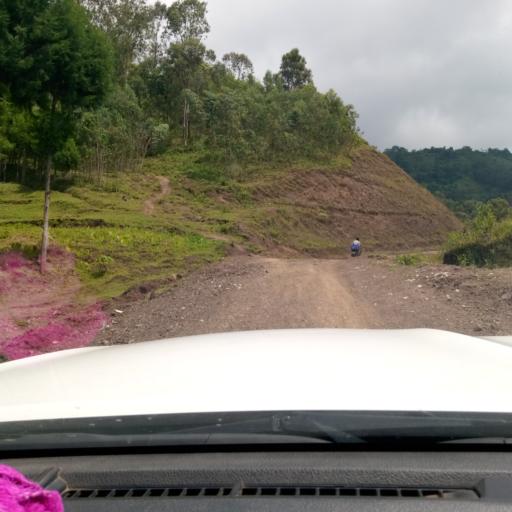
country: ET
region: Southern Nations, Nationalities, and People's Region
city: Arba Minch'
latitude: 6.3141
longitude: 37.3677
